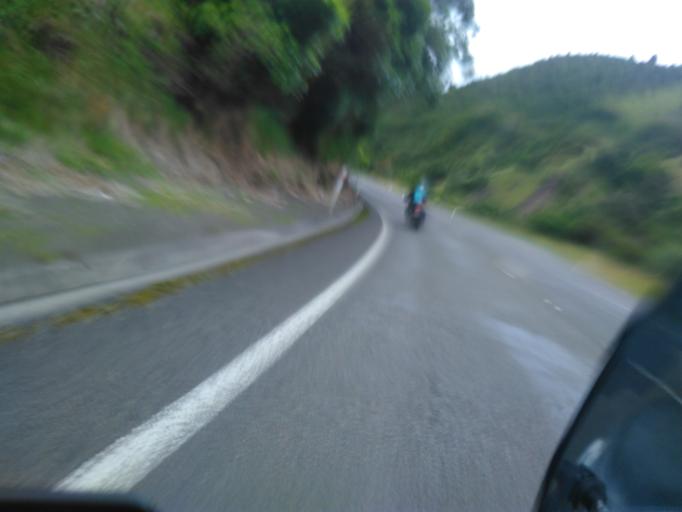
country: NZ
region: Bay of Plenty
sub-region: Opotiki District
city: Opotiki
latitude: -38.3096
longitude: 177.3929
